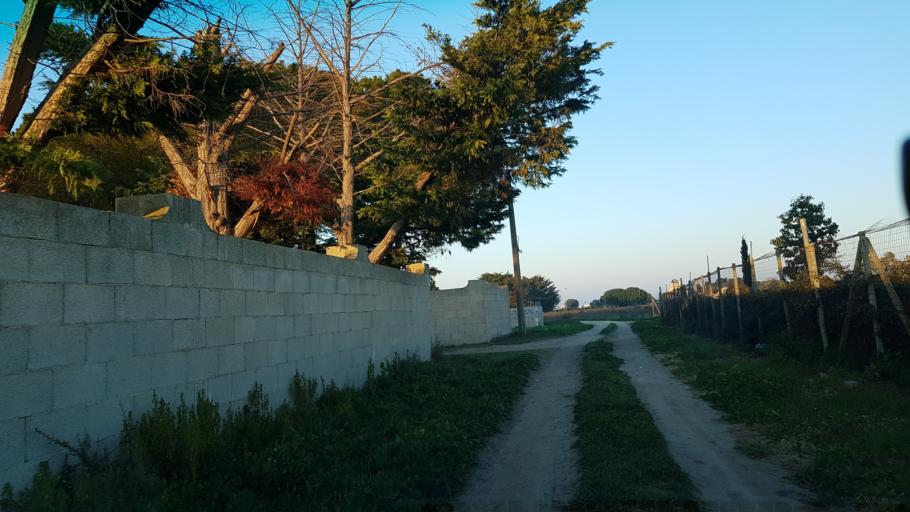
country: IT
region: Apulia
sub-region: Provincia di Brindisi
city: Brindisi
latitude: 40.6520
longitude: 17.9281
